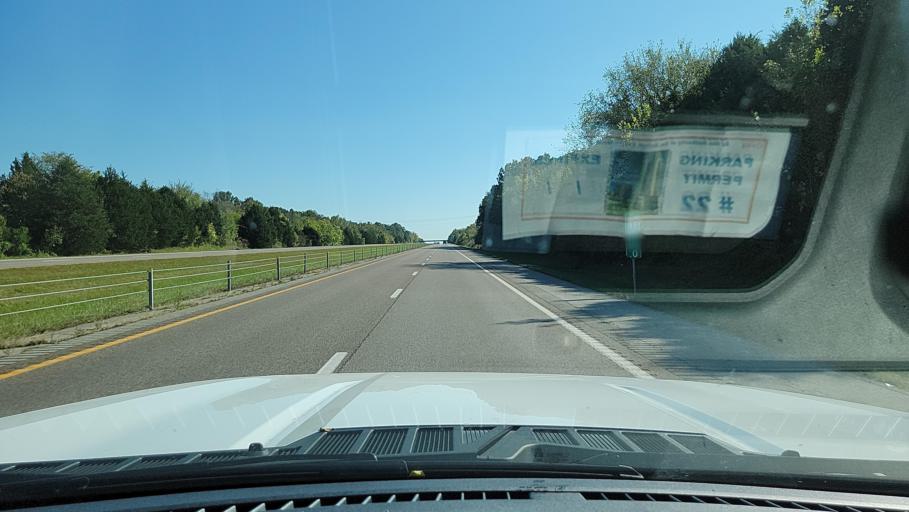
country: US
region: Missouri
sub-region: Jefferson County
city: Crystal City
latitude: 38.1184
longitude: -90.3093
